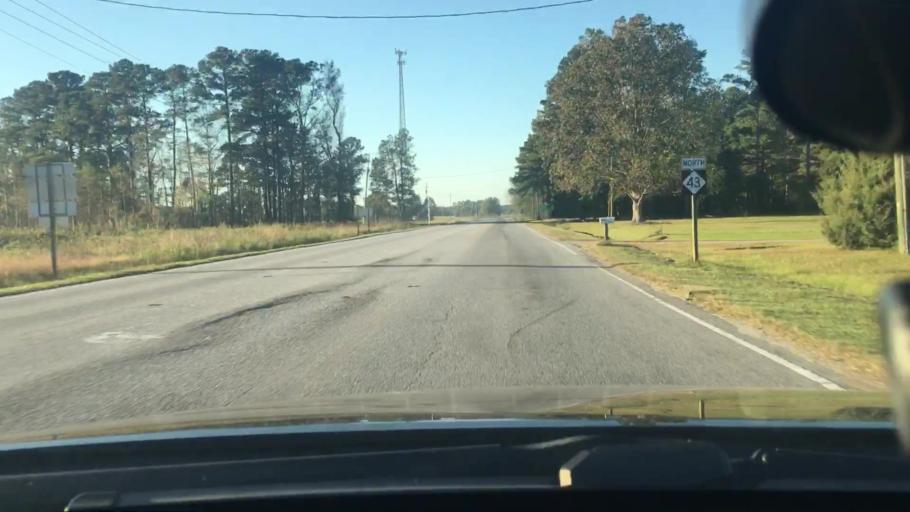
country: US
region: North Carolina
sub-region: Craven County
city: Vanceboro
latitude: 35.4186
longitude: -77.2566
